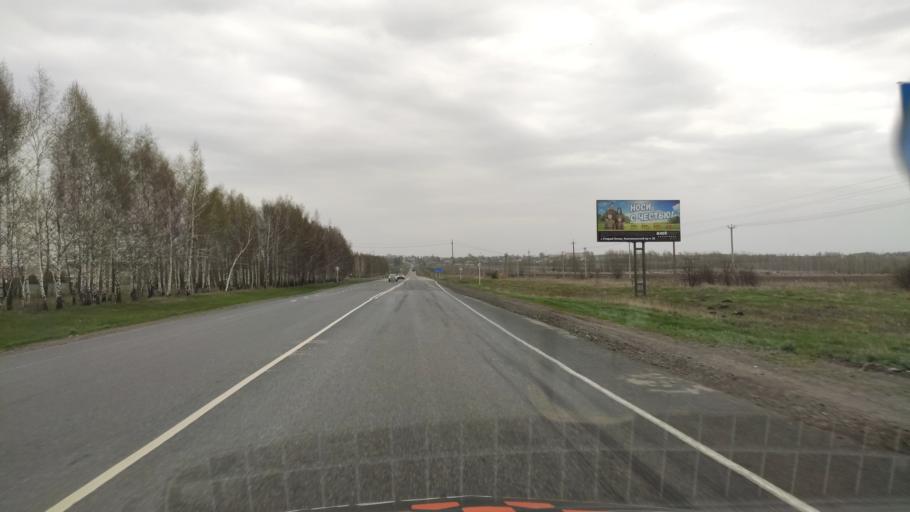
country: RU
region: Kursk
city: Gorshechnoye
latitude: 51.5057
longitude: 37.9932
